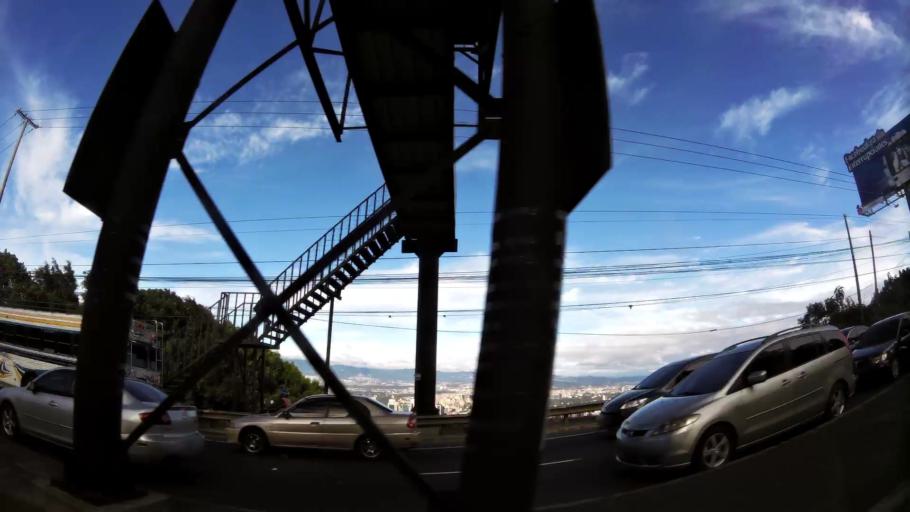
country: GT
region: Guatemala
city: Santa Catarina Pinula
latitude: 14.5747
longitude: -90.4810
